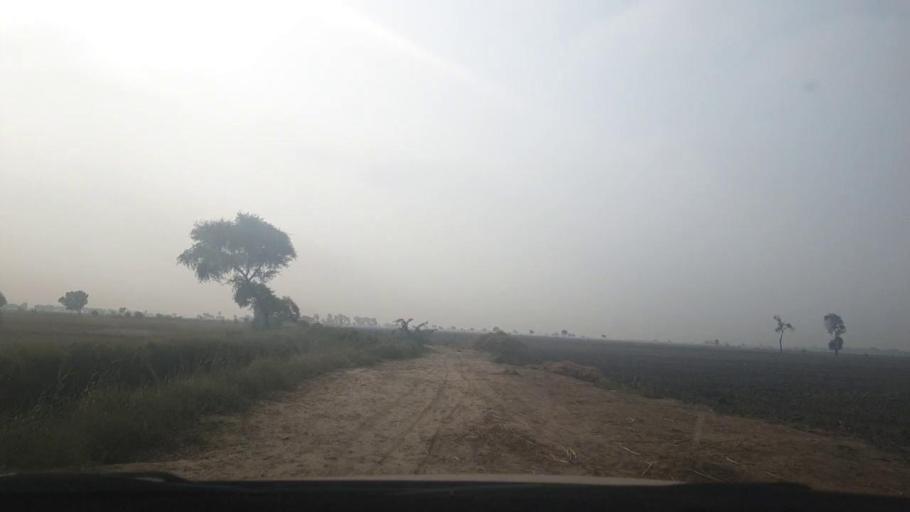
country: PK
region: Sindh
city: Tando Muhammad Khan
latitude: 25.1063
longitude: 68.5235
